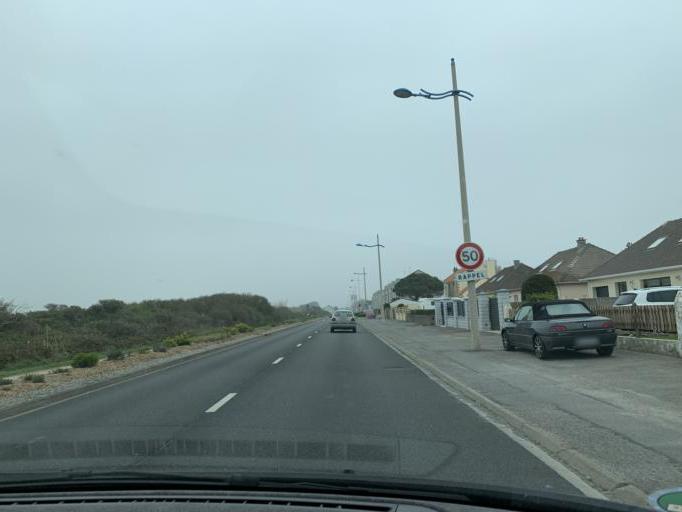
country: FR
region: Nord-Pas-de-Calais
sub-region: Departement du Pas-de-Calais
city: Coquelles
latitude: 50.9564
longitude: 1.8056
